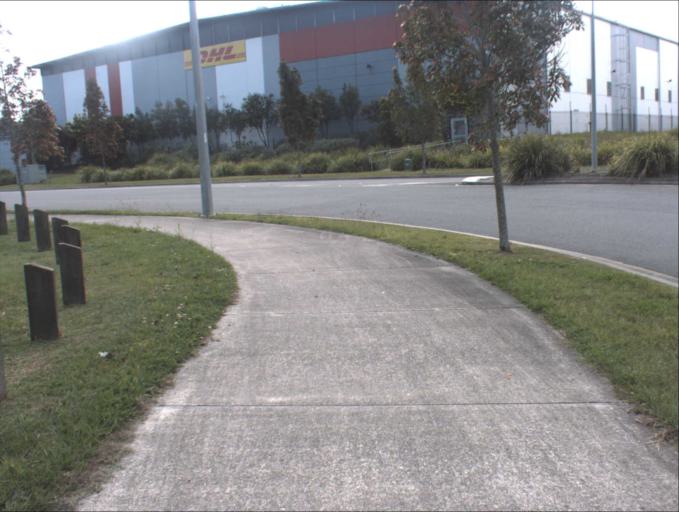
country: AU
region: Queensland
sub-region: Logan
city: Woodridge
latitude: -27.6718
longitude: 153.0750
